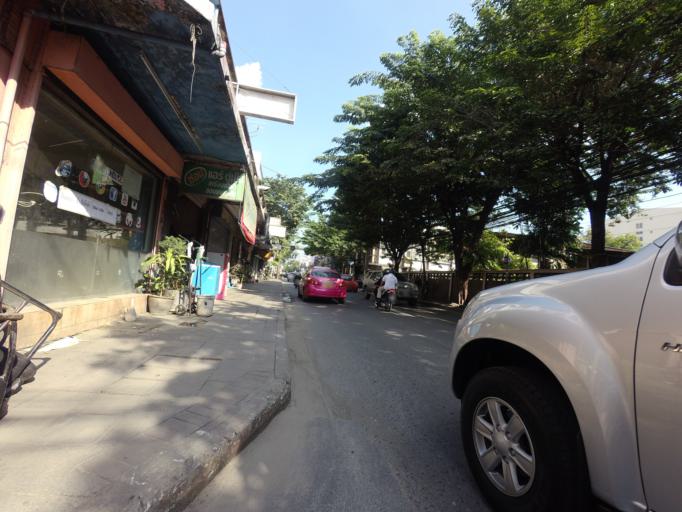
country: TH
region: Bangkok
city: Phaya Thai
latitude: 13.7891
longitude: 100.5553
